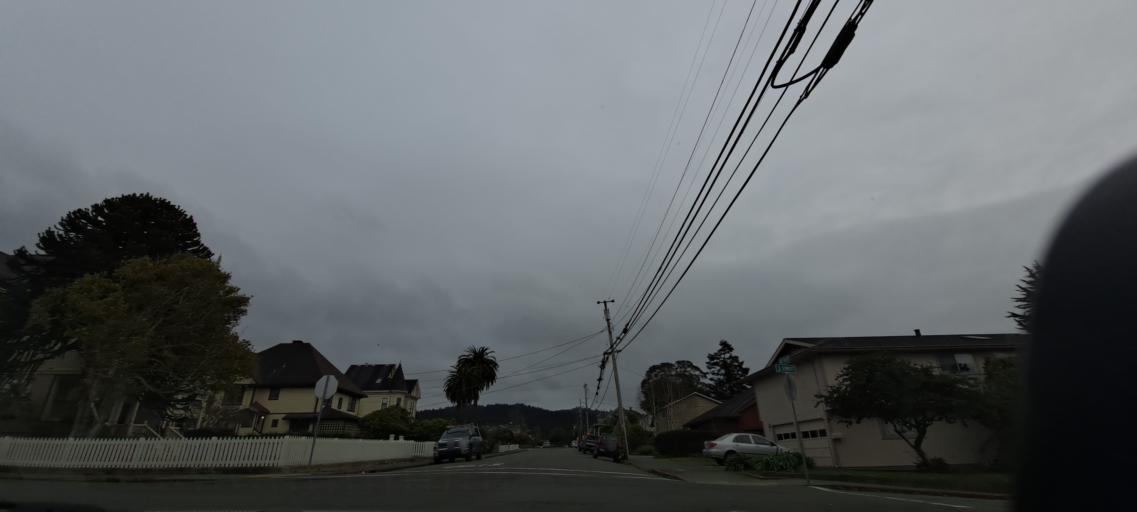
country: US
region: California
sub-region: Humboldt County
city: Arcata
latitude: 40.8735
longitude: -124.0875
